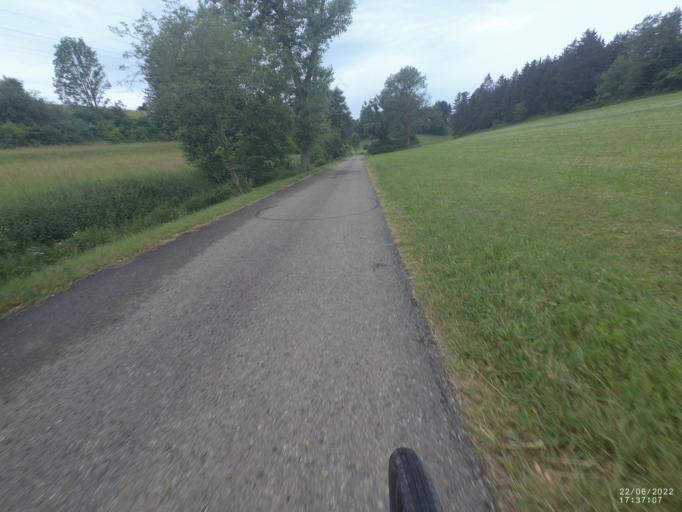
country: DE
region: Baden-Wuerttemberg
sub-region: Regierungsbezirk Stuttgart
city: Gerstetten
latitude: 48.6177
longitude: 10.0037
